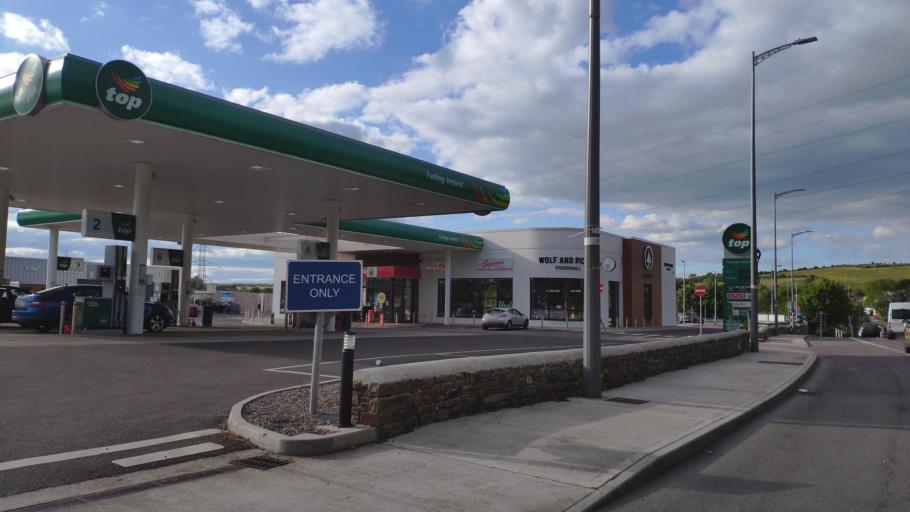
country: IE
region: Munster
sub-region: County Cork
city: Cork
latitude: 51.9138
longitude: -8.4475
